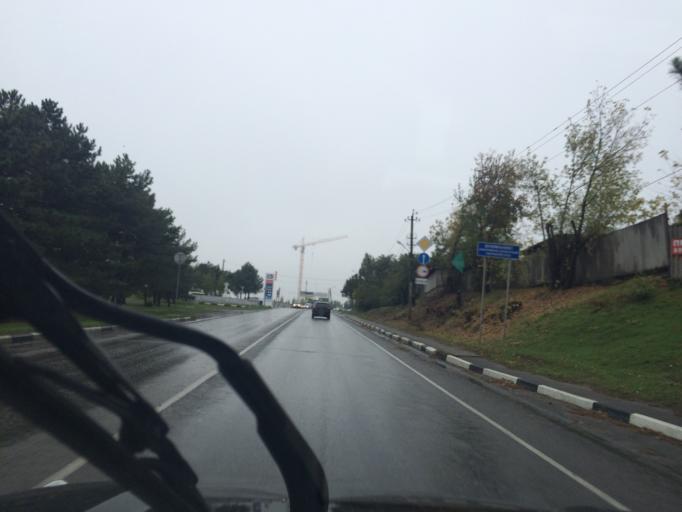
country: RU
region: Rostov
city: Azov
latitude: 47.0897
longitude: 39.4568
